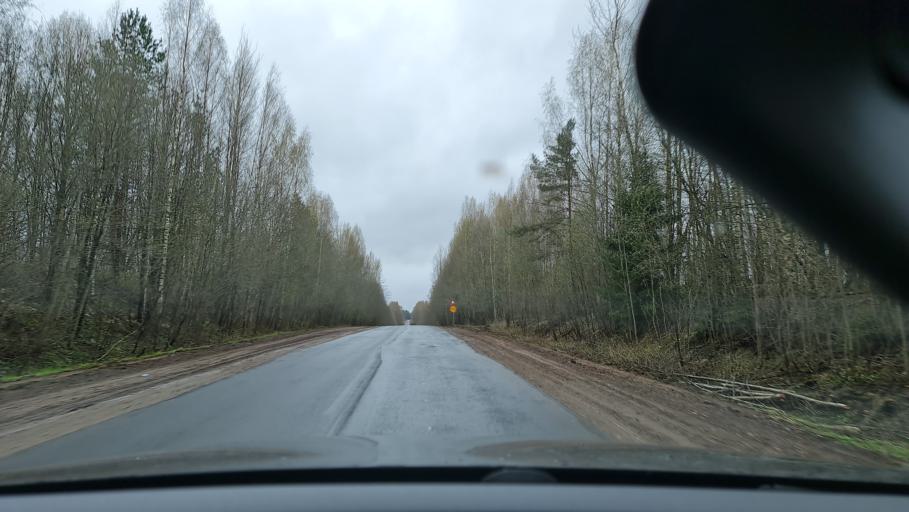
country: RU
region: Novgorod
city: Demyansk
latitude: 57.7390
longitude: 32.5736
